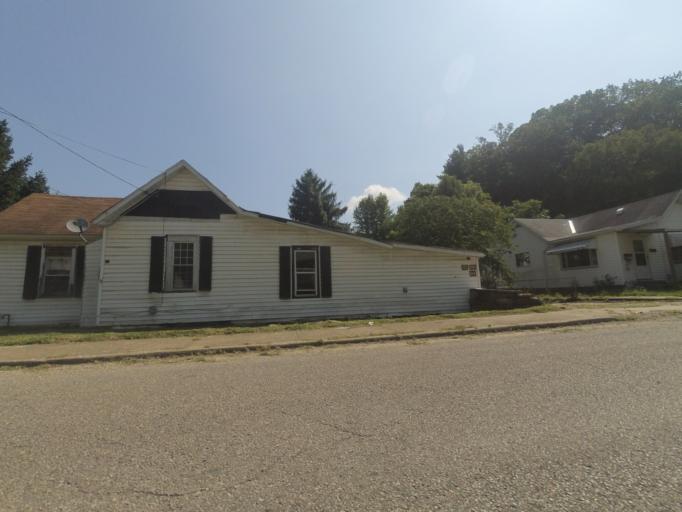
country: US
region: West Virginia
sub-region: Cabell County
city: Huntington
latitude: 38.4148
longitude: -82.4103
